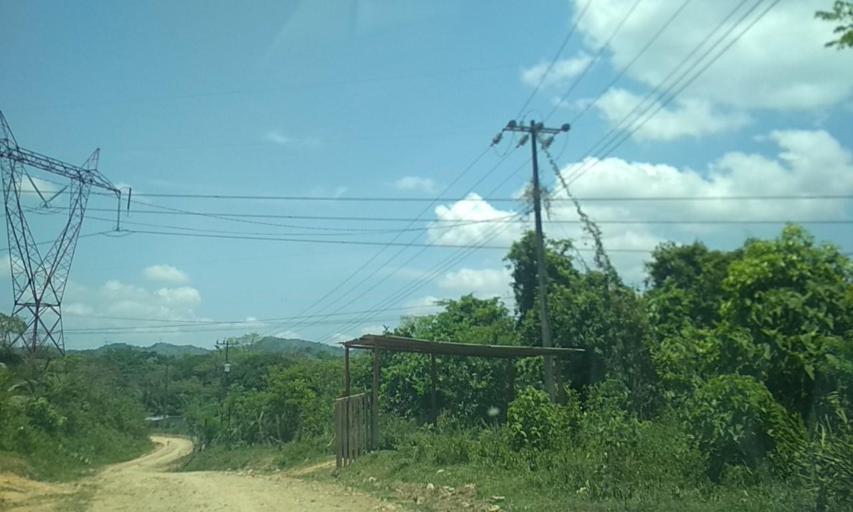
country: MX
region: Chiapas
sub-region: Tecpatan
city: Raudales Malpaso
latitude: 17.3919
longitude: -93.7318
